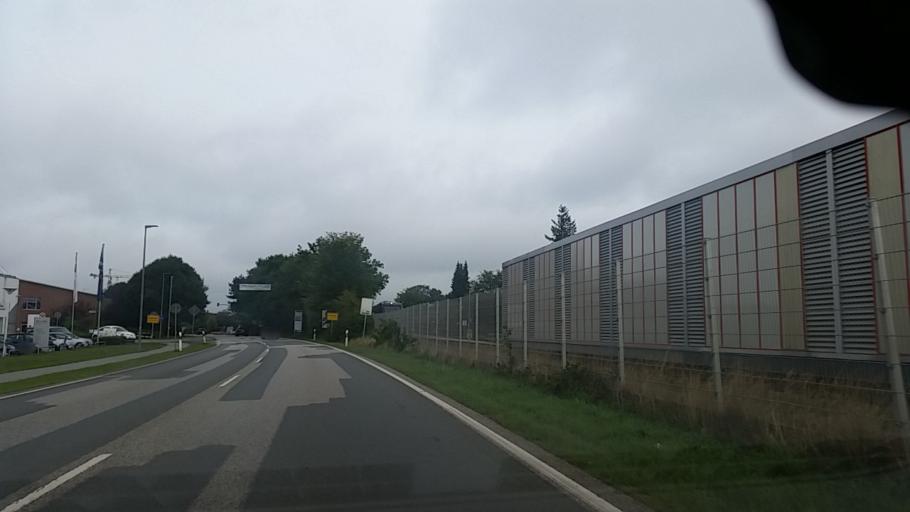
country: DE
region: Schleswig-Holstein
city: Oersdorf
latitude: 53.8308
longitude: 9.9719
